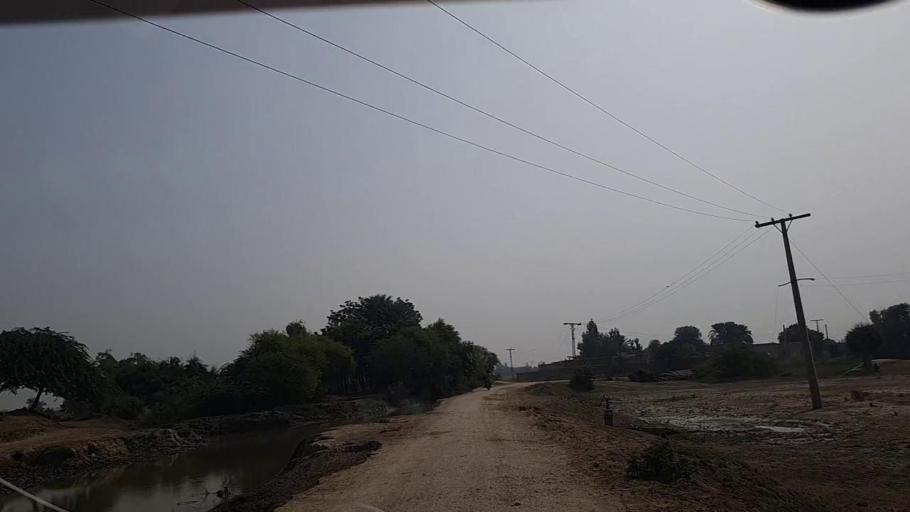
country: PK
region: Sindh
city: Garhi Yasin
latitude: 27.9234
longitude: 68.5693
